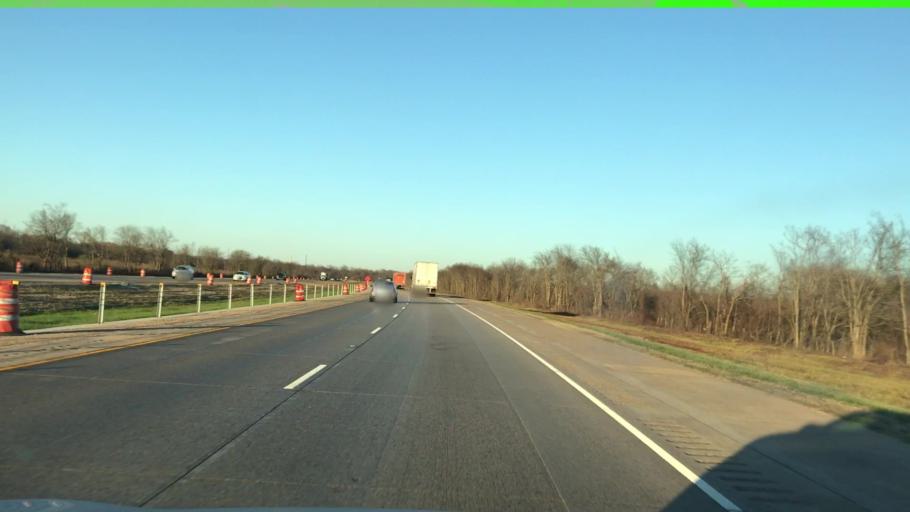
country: US
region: Arkansas
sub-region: Miller County
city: Texarkana
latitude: 33.5753
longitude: -93.8464
